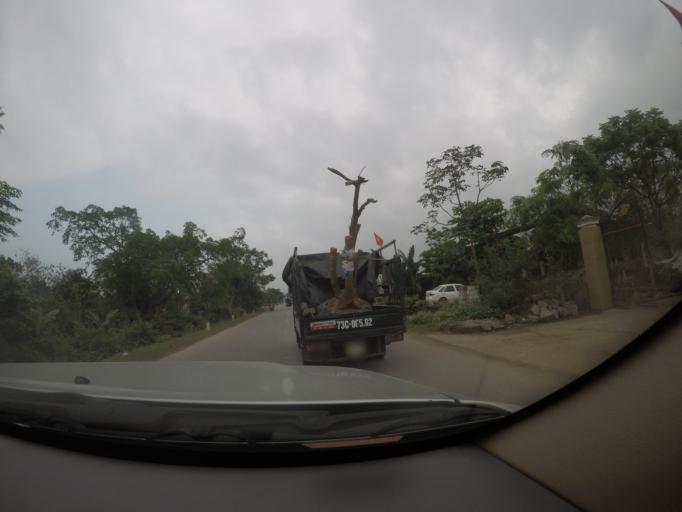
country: VN
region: Quang Binh
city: Kien Giang
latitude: 17.2263
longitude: 106.7024
